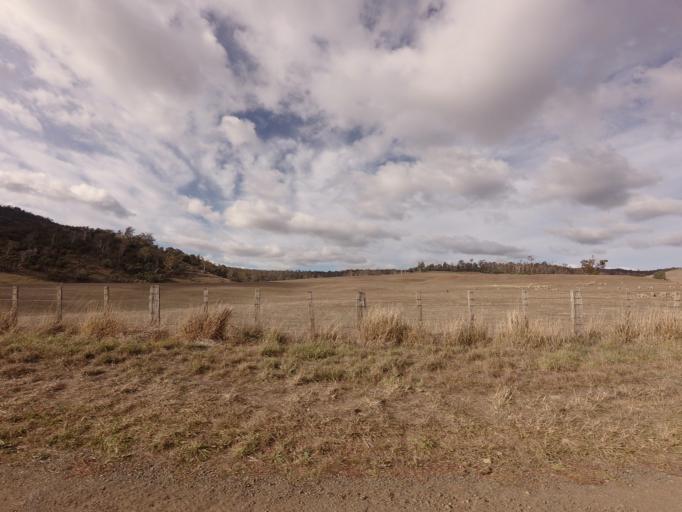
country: AU
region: Tasmania
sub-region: Brighton
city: Bridgewater
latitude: -42.4680
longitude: 147.2797
